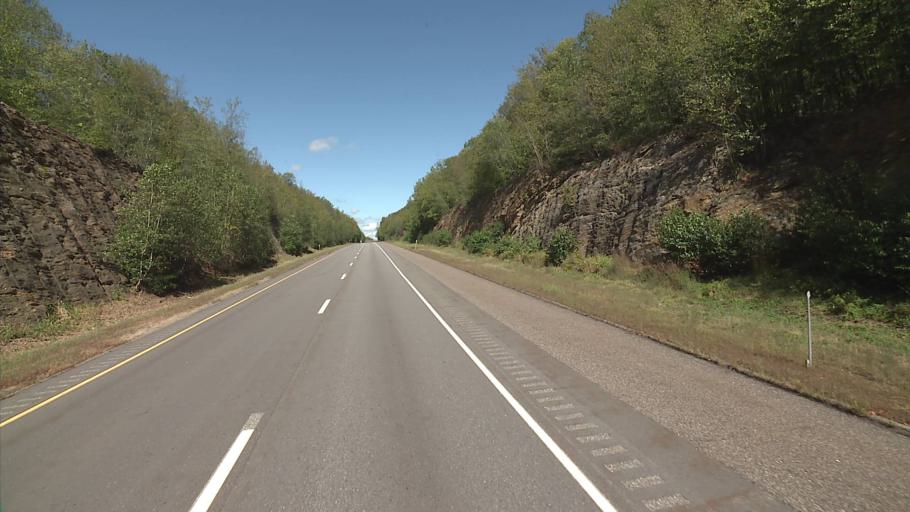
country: US
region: Connecticut
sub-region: New London County
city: Colchester
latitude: 41.5332
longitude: -72.3093
